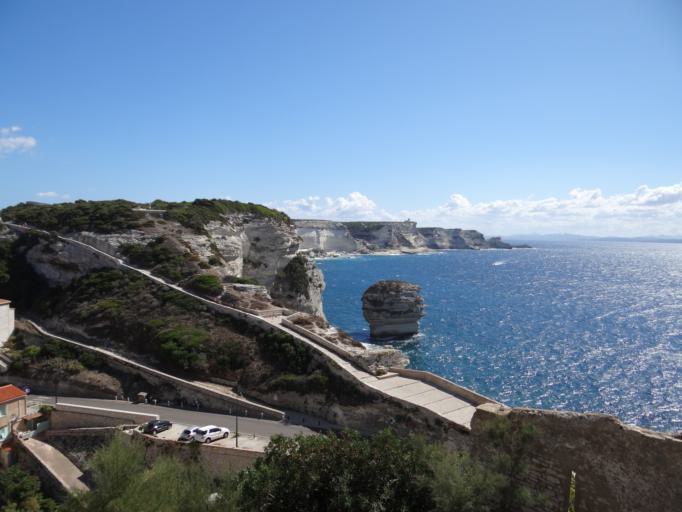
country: FR
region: Corsica
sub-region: Departement de la Corse-du-Sud
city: Bonifacio
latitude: 41.3875
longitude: 9.1601
